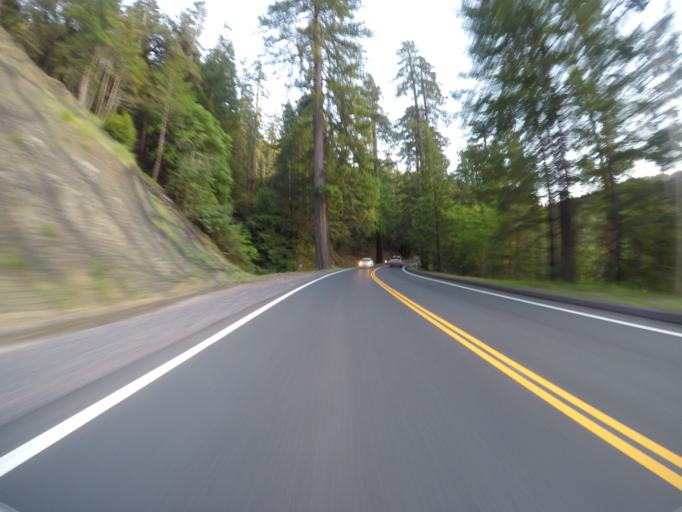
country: US
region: California
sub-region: Humboldt County
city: Redway
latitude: 39.9050
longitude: -123.7493
